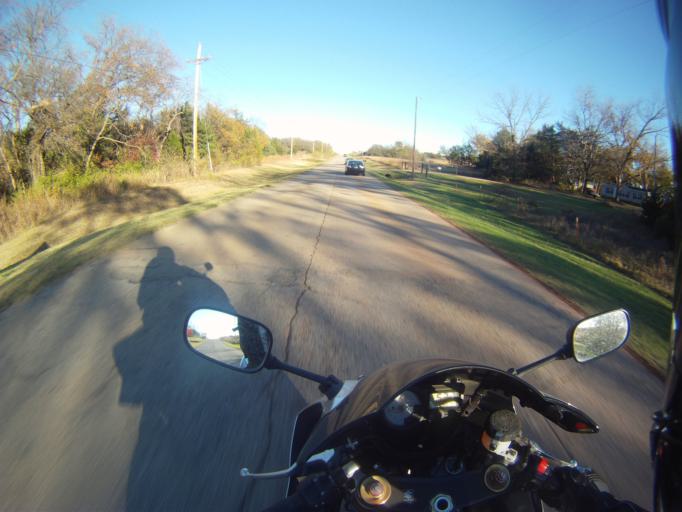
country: US
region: Oklahoma
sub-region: Payne County
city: Stillwater
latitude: 36.1303
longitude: -97.1204
